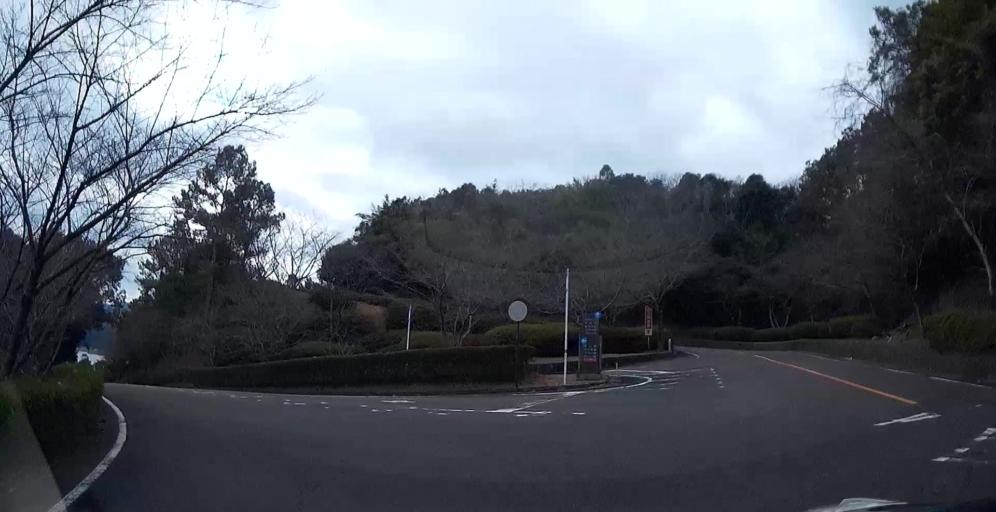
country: JP
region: Kumamoto
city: Minamata
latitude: 32.3646
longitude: 130.4925
